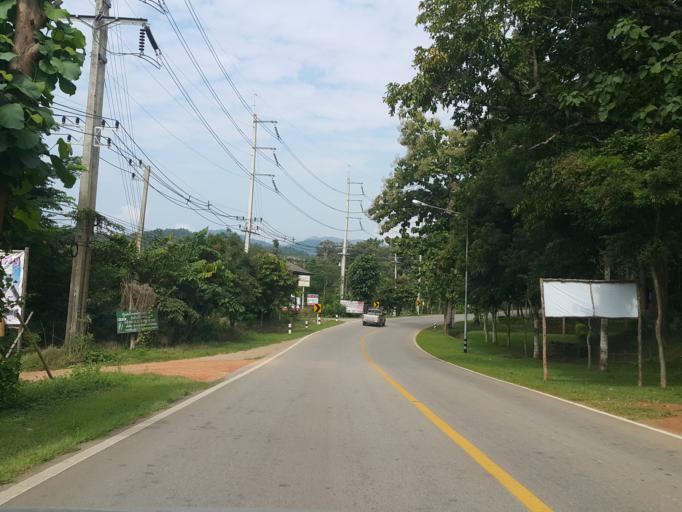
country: TH
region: Mae Hong Son
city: Mae Hong Son
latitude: 19.3676
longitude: 97.9654
